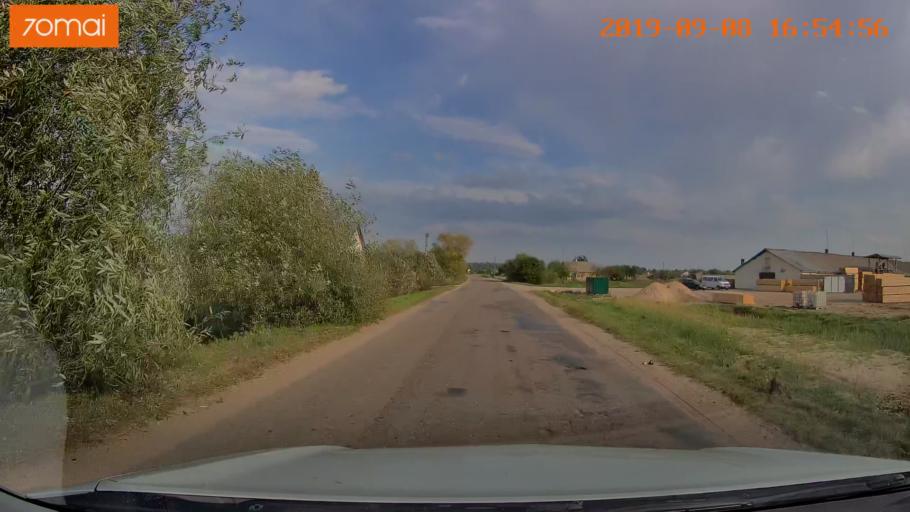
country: BY
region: Grodnenskaya
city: Hrodna
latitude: 53.7493
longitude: 23.9250
